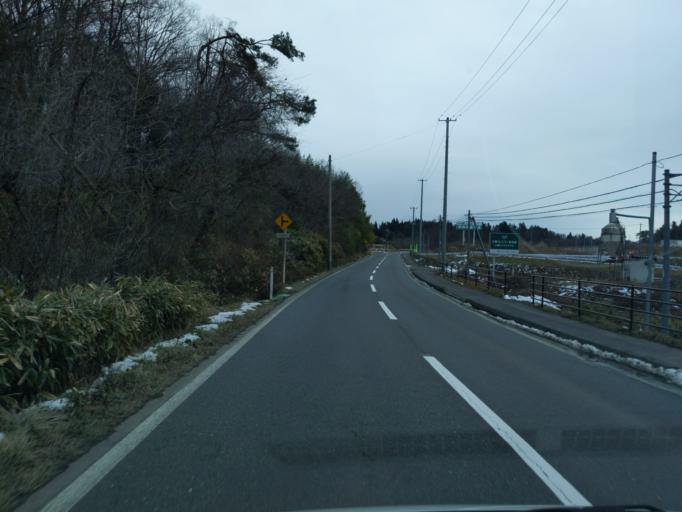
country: JP
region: Iwate
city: Mizusawa
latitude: 39.1539
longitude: 141.2131
